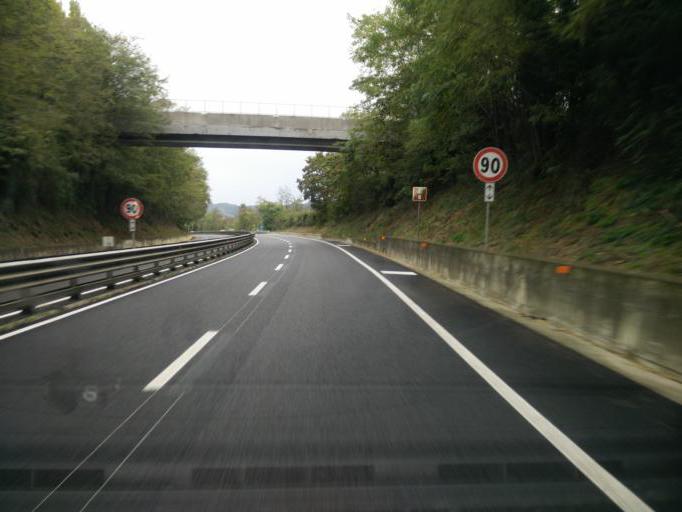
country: IT
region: Tuscany
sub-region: Provincia di Siena
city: Bellavista
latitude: 43.4389
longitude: 11.1490
